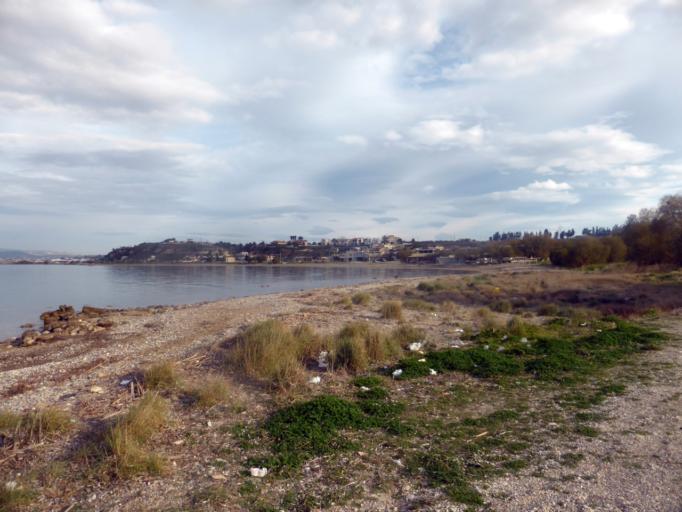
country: GR
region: Peloponnese
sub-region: Nomos Korinthias
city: Arkhaia Korinthos
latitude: 37.9328
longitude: 22.8937
